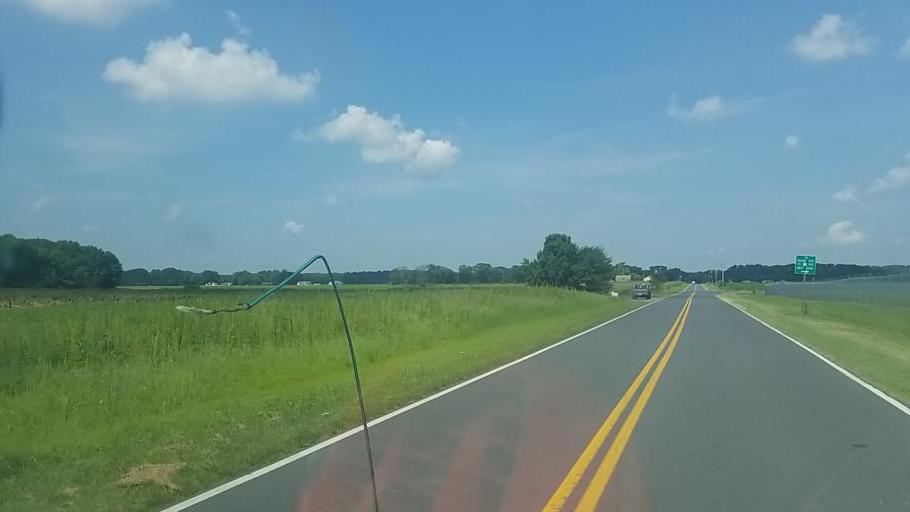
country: US
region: Maryland
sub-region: Wicomico County
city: Salisbury
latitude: 38.3460
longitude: -75.5198
